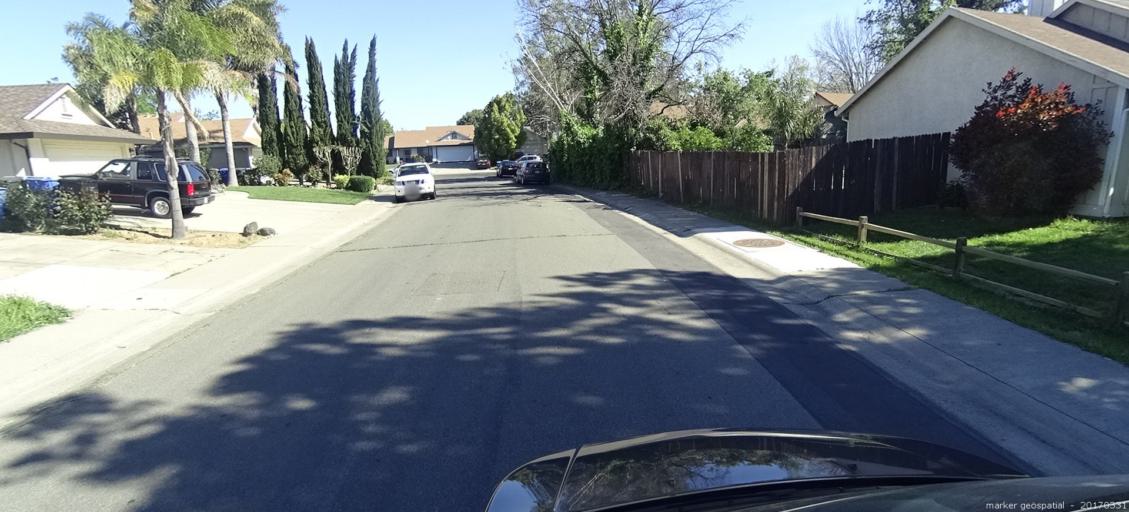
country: US
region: California
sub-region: Sacramento County
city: Parkway
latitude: 38.4697
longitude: -121.4449
